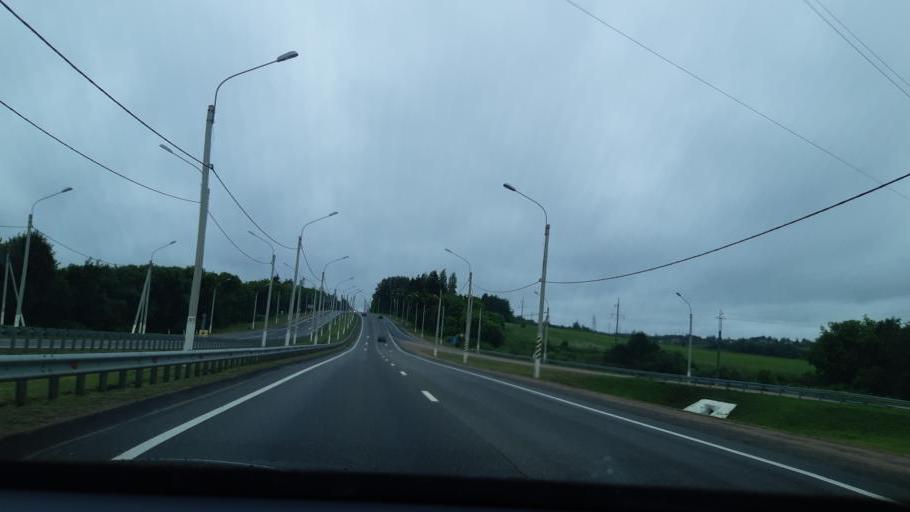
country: RU
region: Smolensk
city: Talashkino
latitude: 54.7082
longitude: 32.1155
